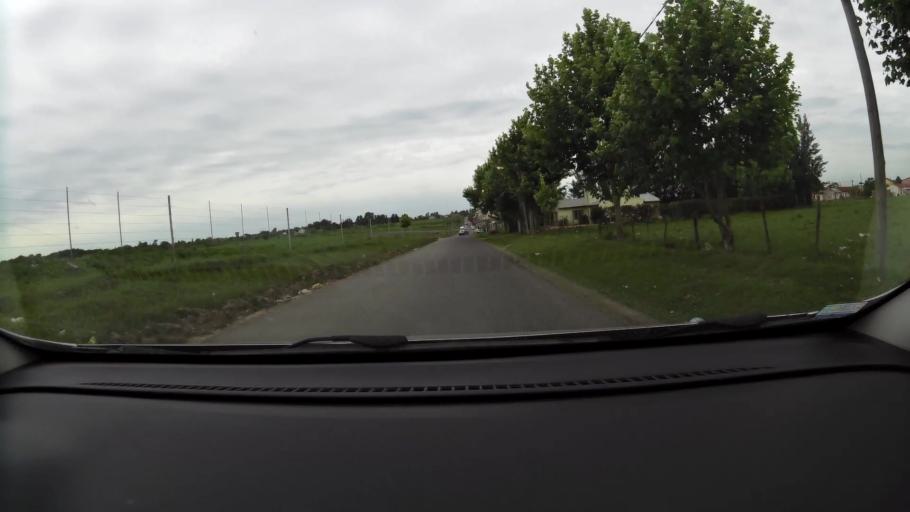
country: AR
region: Buenos Aires
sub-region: Partido de Campana
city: Campana
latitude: -34.2032
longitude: -58.9471
